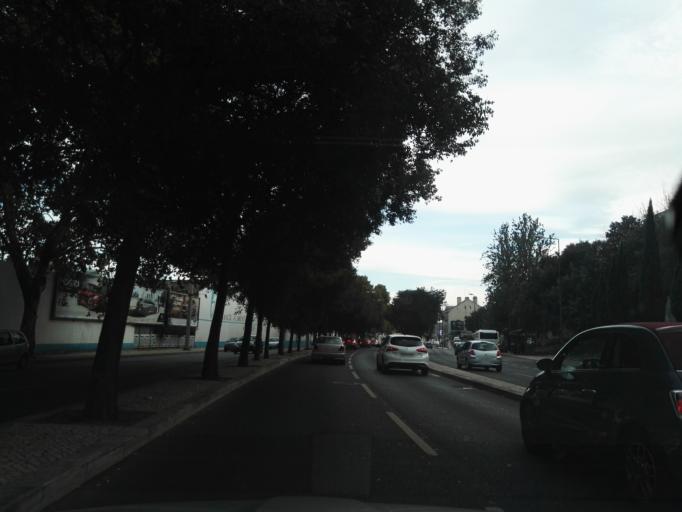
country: PT
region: Setubal
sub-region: Almada
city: Almada
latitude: 38.7091
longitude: -9.1738
